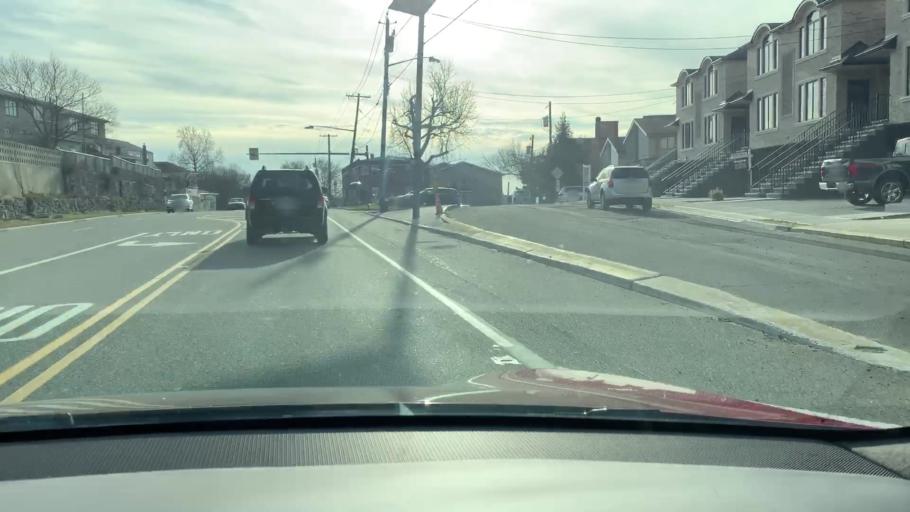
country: US
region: New Jersey
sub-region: Bergen County
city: Palisades Park
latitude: 40.8409
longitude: -73.9887
